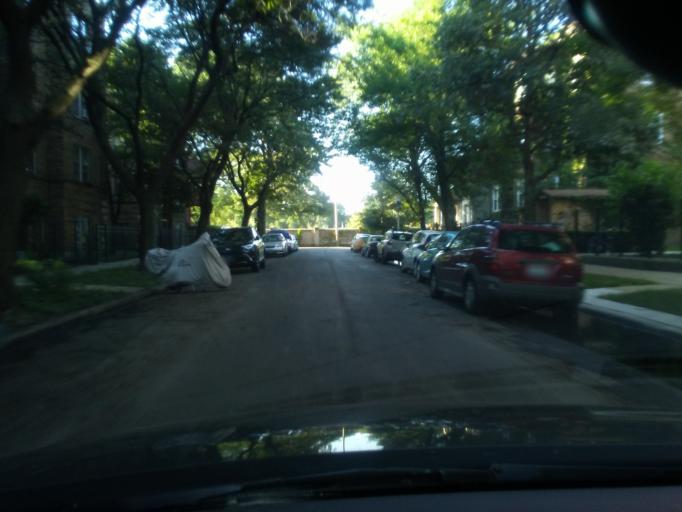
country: US
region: Illinois
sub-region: Cook County
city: Lincolnwood
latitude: 41.9724
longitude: -87.6648
